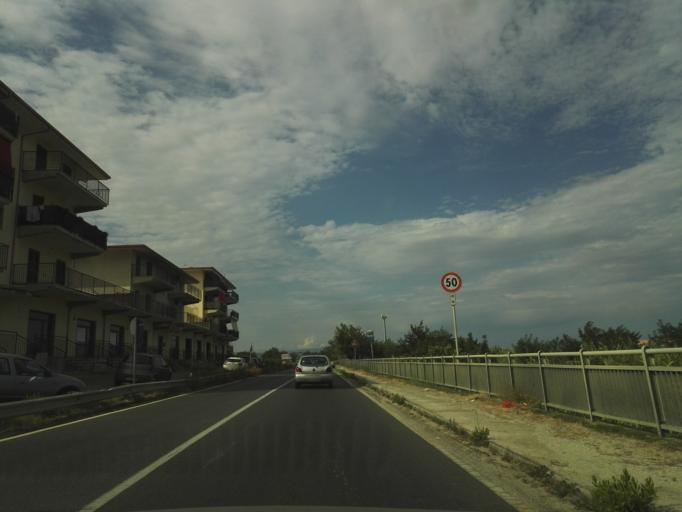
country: IT
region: Calabria
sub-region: Provincia di Catanzaro
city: Marina di Davoli
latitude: 38.6520
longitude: 16.5476
